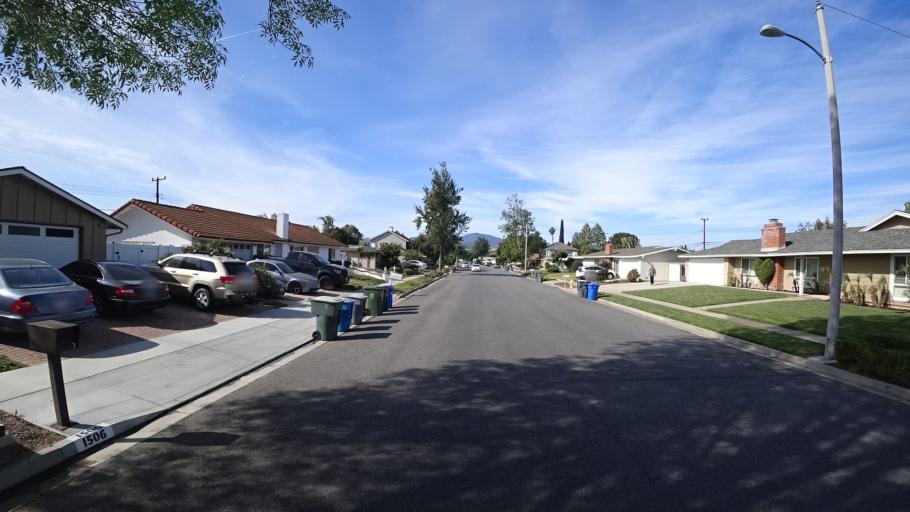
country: US
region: California
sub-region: Ventura County
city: Thousand Oaks
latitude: 34.1981
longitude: -118.8724
